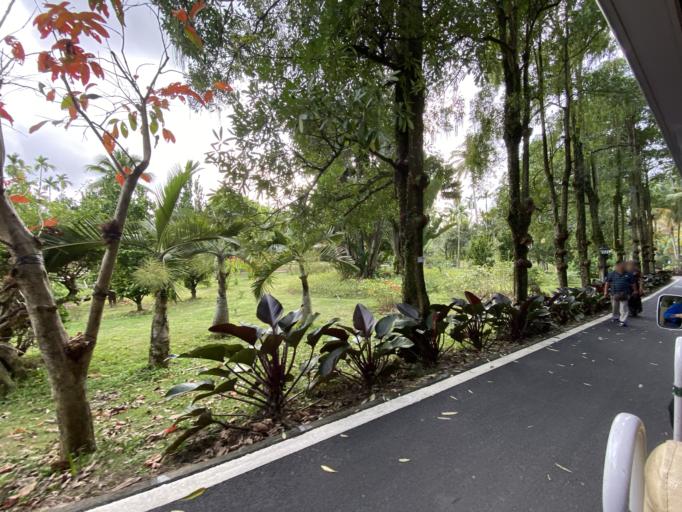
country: CN
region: Hainan
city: Nanqiao
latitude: 18.7344
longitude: 110.1934
